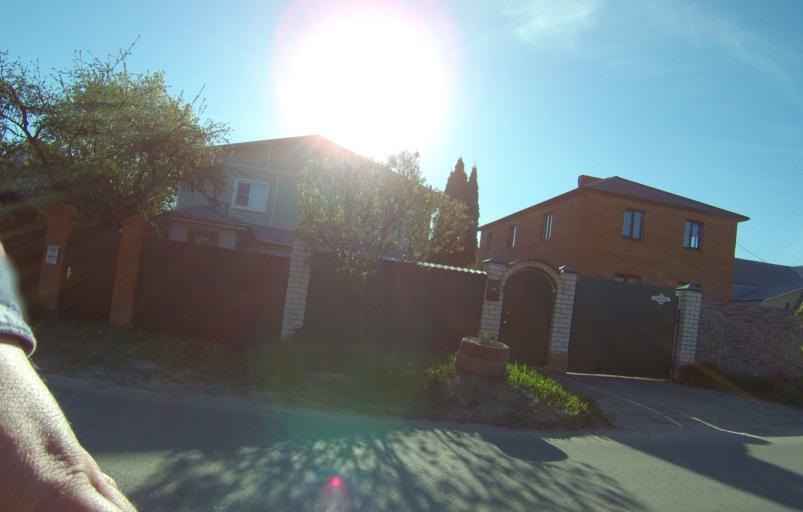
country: RU
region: Moskovskaya
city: Ramenskoye
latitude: 55.5473
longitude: 38.1961
